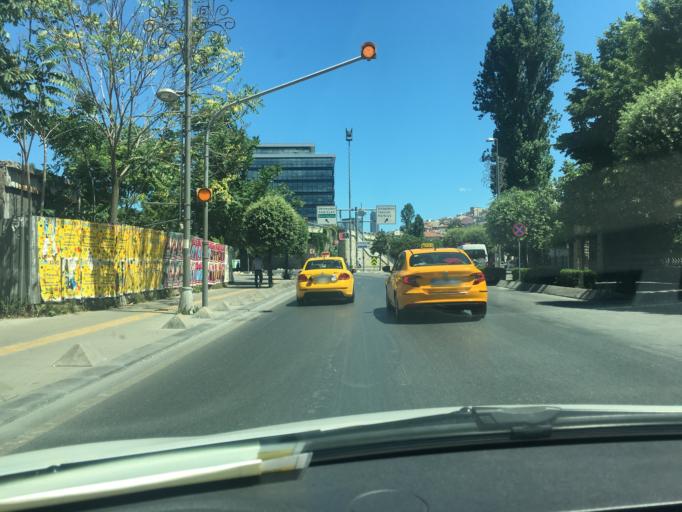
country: TR
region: Istanbul
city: Eminoenue
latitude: 41.0373
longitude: 28.9709
